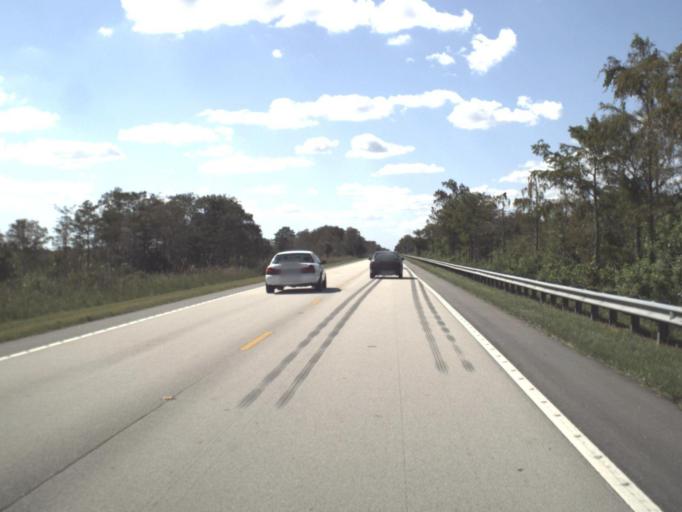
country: US
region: Florida
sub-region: Collier County
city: Immokalee
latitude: 25.8615
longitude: -81.0787
